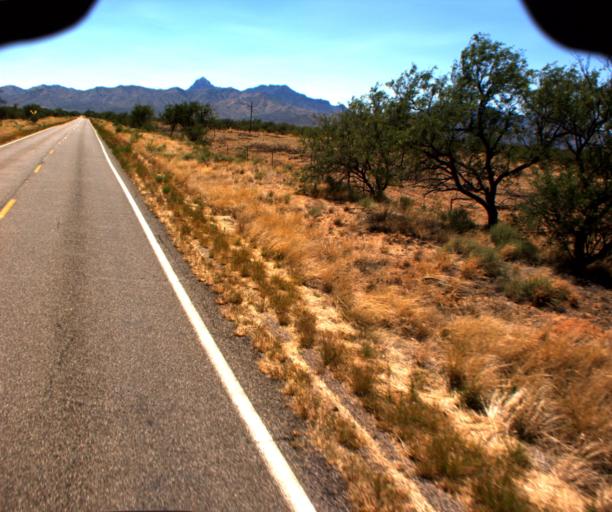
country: US
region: Arizona
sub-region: Pima County
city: Three Points
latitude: 31.8255
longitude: -111.4304
